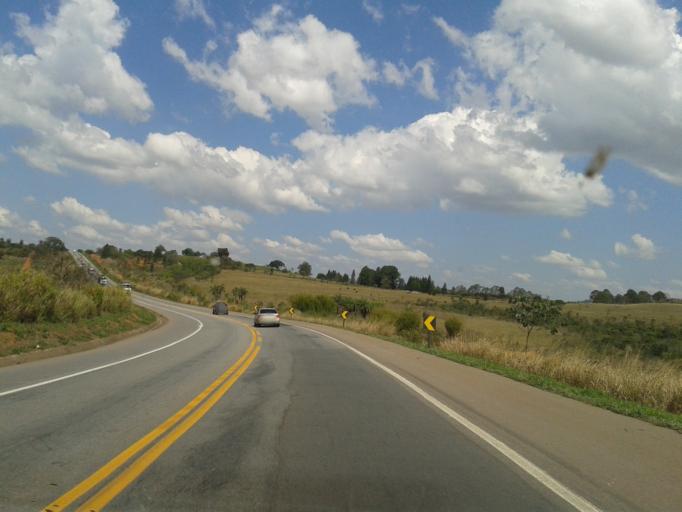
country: BR
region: Minas Gerais
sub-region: Campos Altos
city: Campos Altos
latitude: -19.6910
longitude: -46.0380
